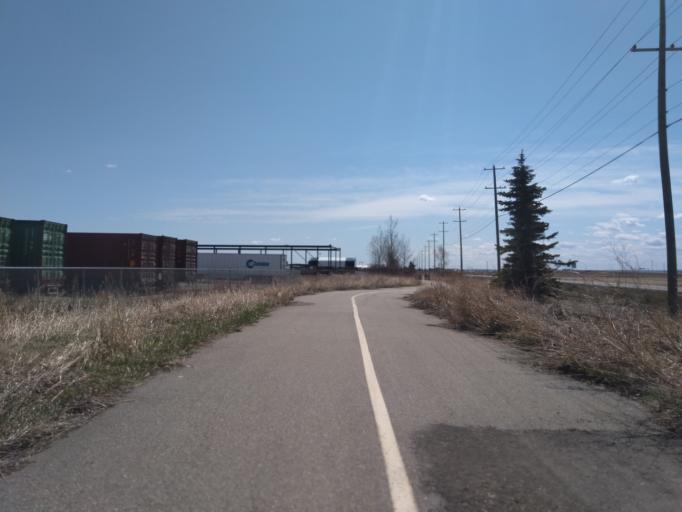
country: CA
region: Alberta
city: Chestermere
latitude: 50.9688
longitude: -113.9115
